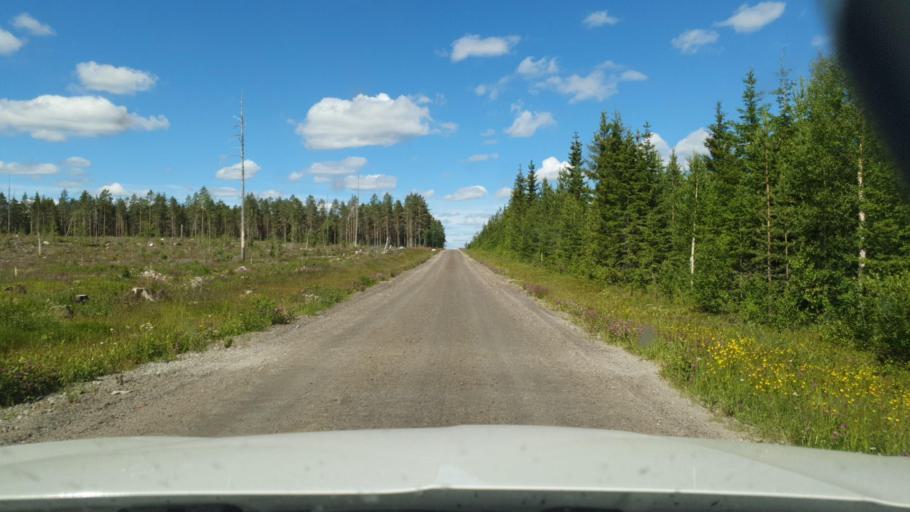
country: SE
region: Vaesterbotten
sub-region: Skelleftea Kommun
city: Byske
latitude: 65.1311
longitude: 21.1972
